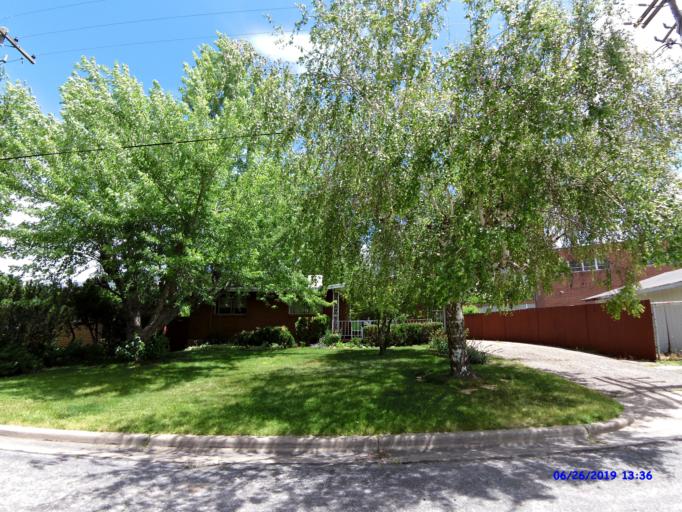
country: US
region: Utah
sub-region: Weber County
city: South Ogden
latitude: 41.2046
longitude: -111.9597
